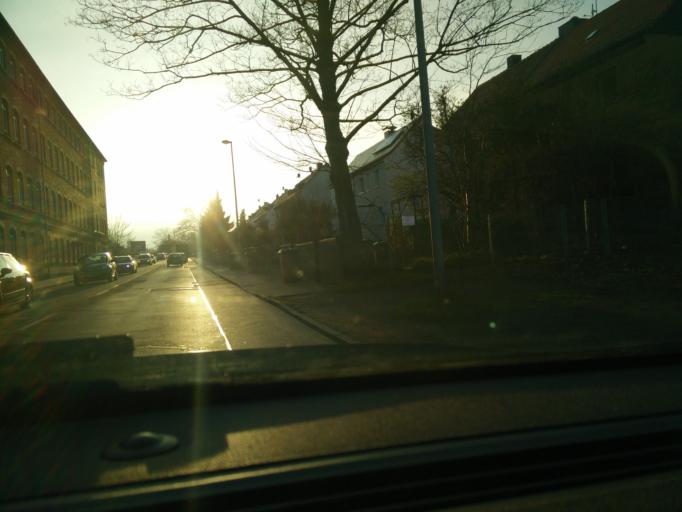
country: DE
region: Saxony
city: Taucha
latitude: 51.3303
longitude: 12.4405
